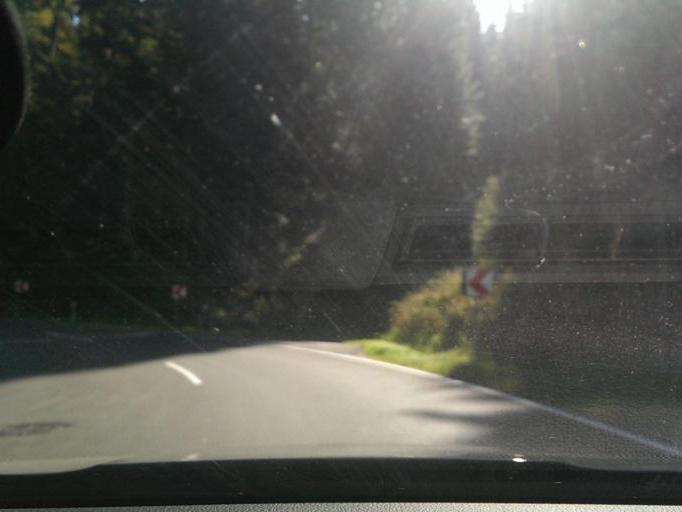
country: DE
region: Baden-Wuerttemberg
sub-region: Karlsruhe Region
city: Bad Herrenalb
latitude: 48.8011
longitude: 8.4634
